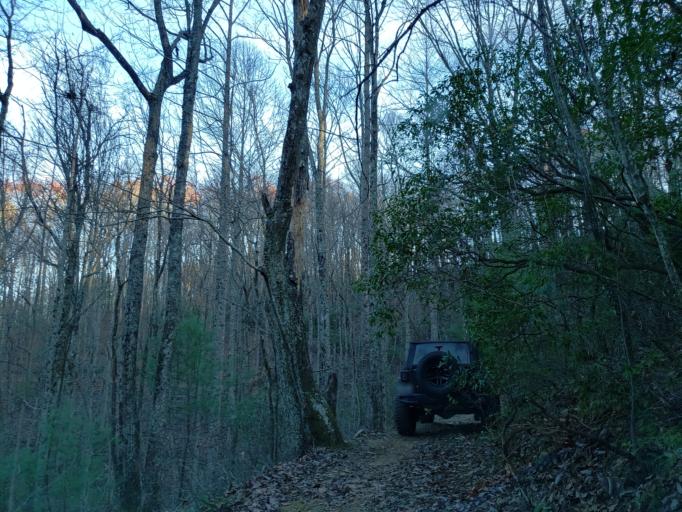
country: US
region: Georgia
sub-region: Lumpkin County
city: Dahlonega
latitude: 34.6672
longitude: -84.1034
